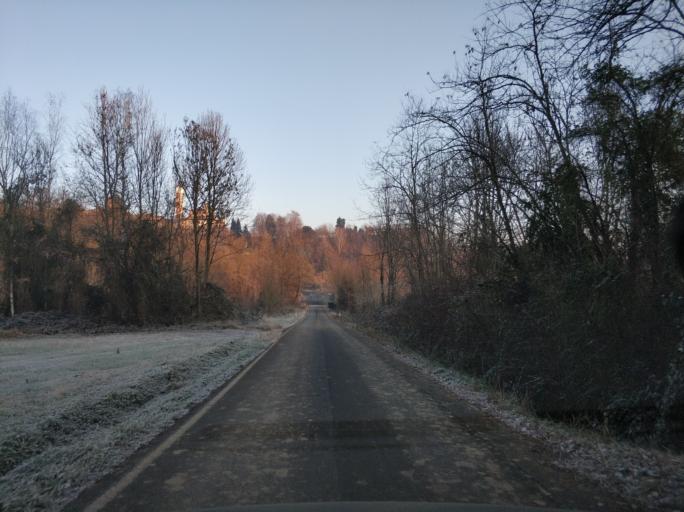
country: IT
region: Piedmont
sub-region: Provincia di Torino
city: Barbania
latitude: 45.2866
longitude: 7.6308
